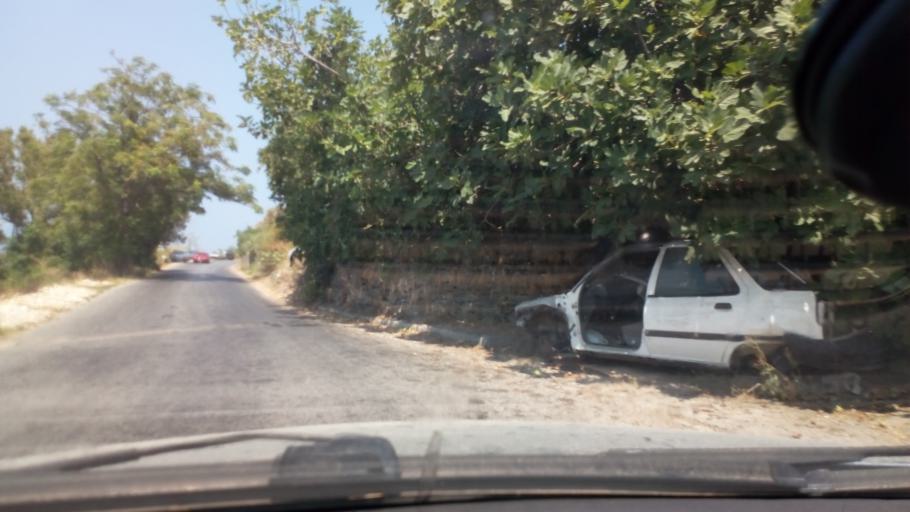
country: GR
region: North Aegean
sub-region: Nomos Samou
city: Agios Kirykos
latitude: 37.6288
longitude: 26.1626
